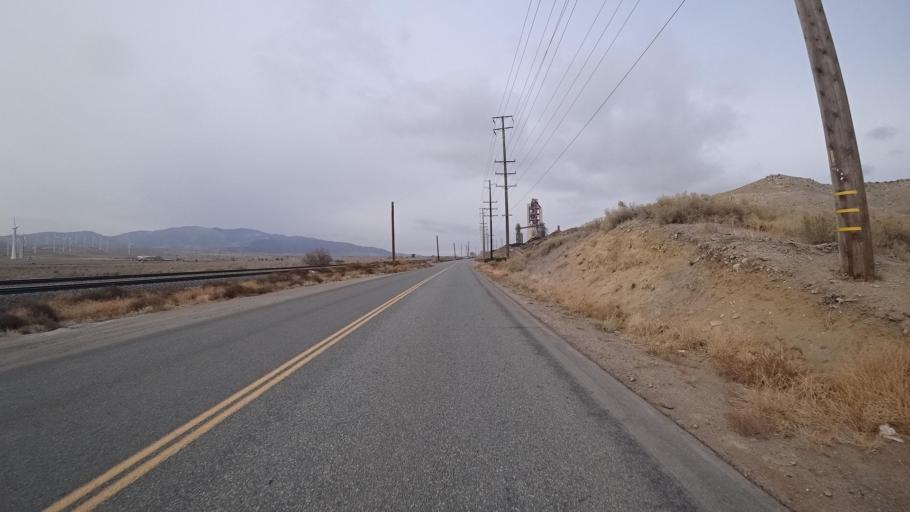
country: US
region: California
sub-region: Kern County
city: Tehachapi
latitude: 35.1210
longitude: -118.3591
